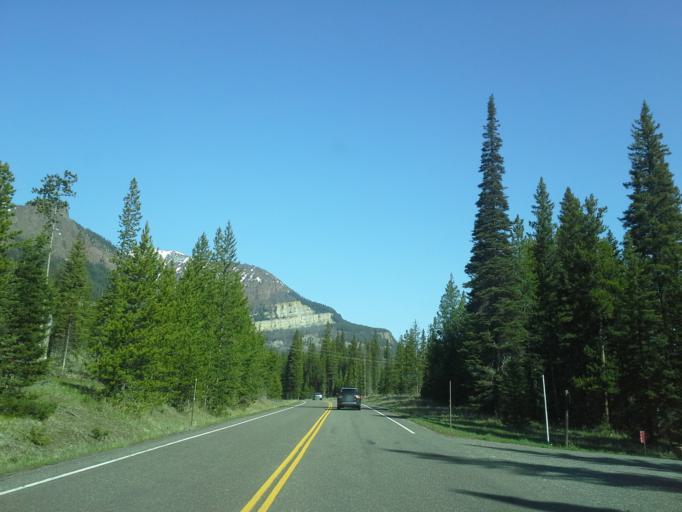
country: US
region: Montana
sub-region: Carbon County
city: Red Lodge
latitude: 44.9739
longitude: -109.8333
